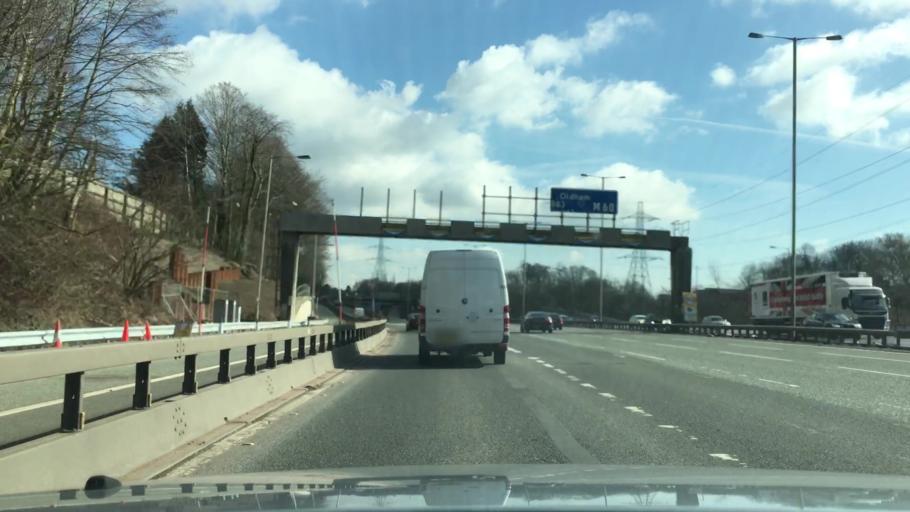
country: GB
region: England
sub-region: Borough of Bury
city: Prestwich
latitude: 53.5376
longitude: -2.2952
